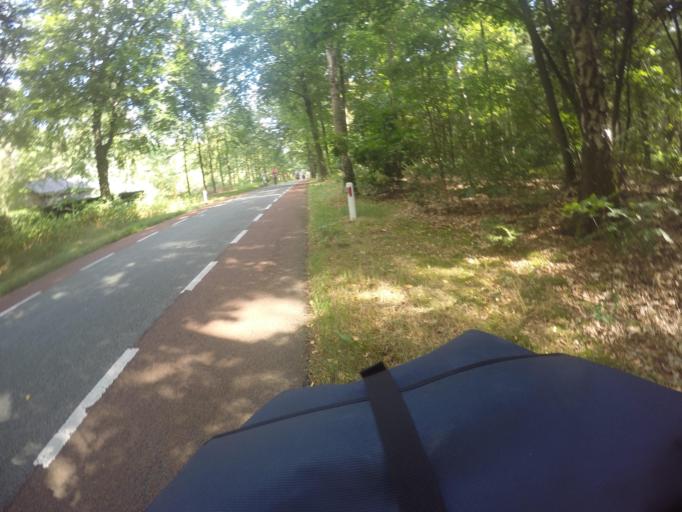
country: NL
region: Gelderland
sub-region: Gemeente Renkum
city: Oosterbeek
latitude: 51.9987
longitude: 5.8267
